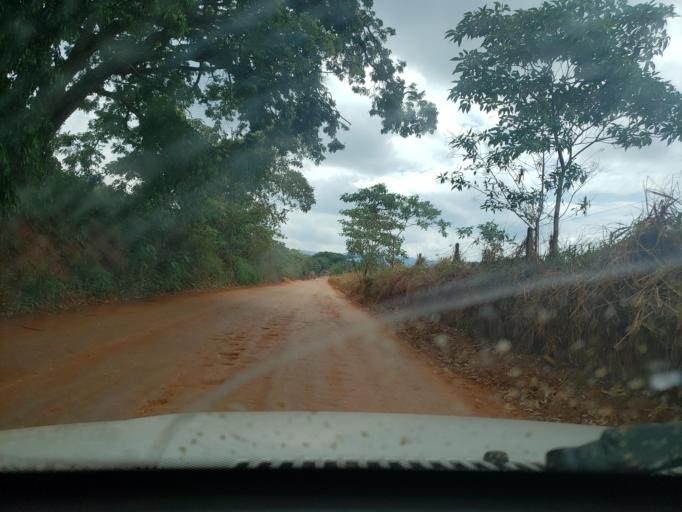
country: BR
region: Minas Gerais
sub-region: Boa Esperanca
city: Boa Esperanca
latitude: -20.9807
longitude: -45.5957
